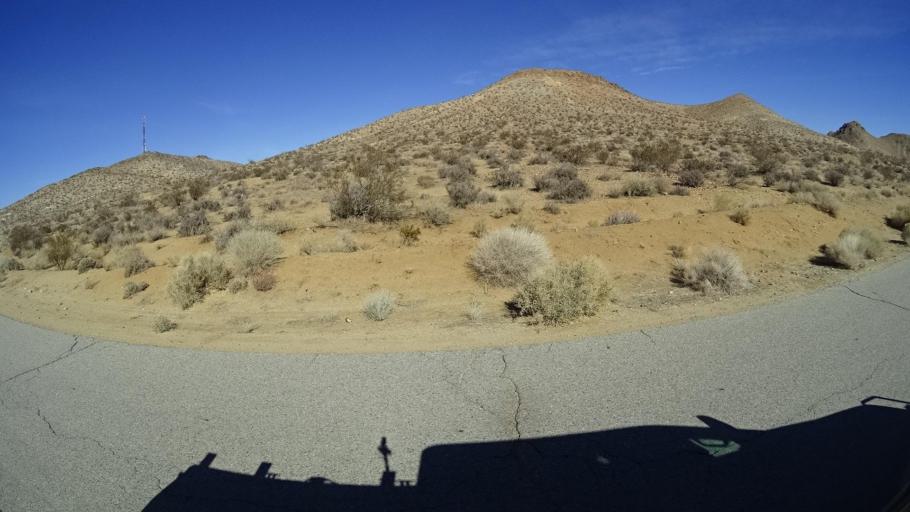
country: US
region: California
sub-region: Kern County
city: Ridgecrest
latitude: 35.3569
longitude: -117.6365
